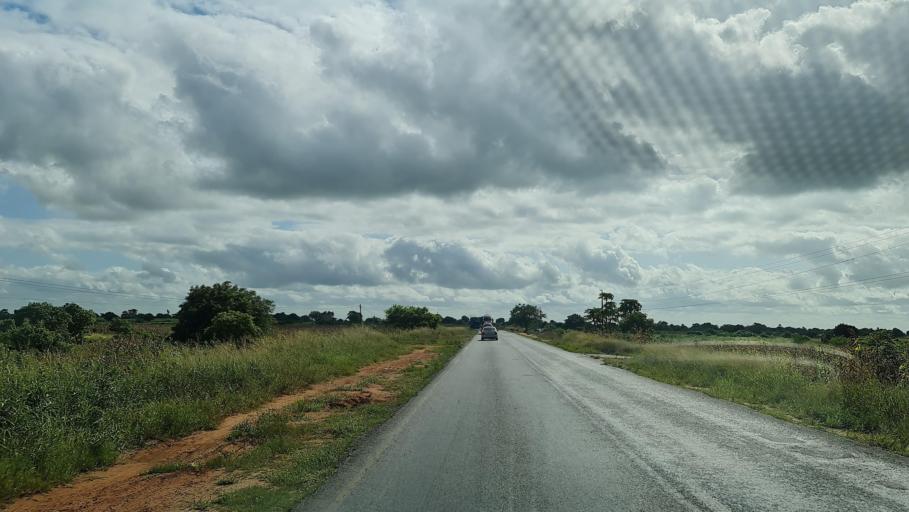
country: MZ
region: Gaza
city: Macia
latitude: -25.0905
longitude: 32.8401
